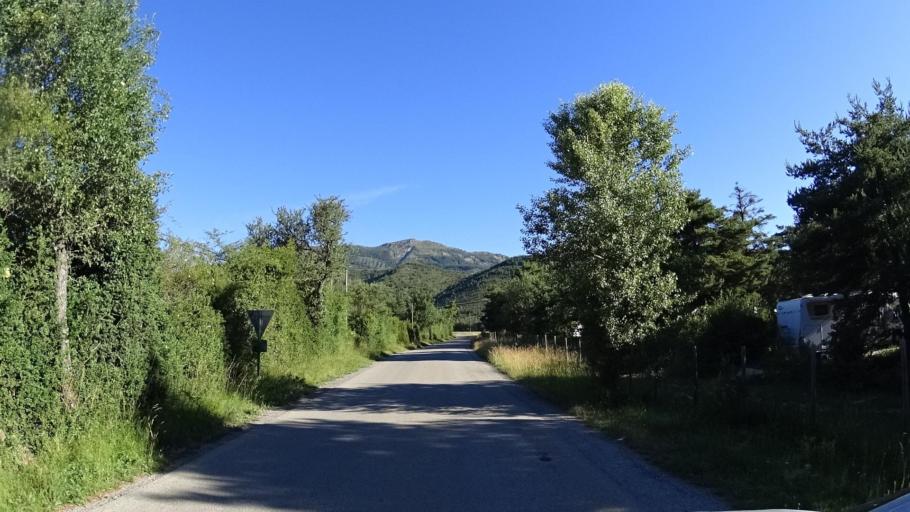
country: FR
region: Provence-Alpes-Cote d'Azur
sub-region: Departement des Alpes-de-Haute-Provence
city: Castellane
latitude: 43.8718
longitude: 6.5113
